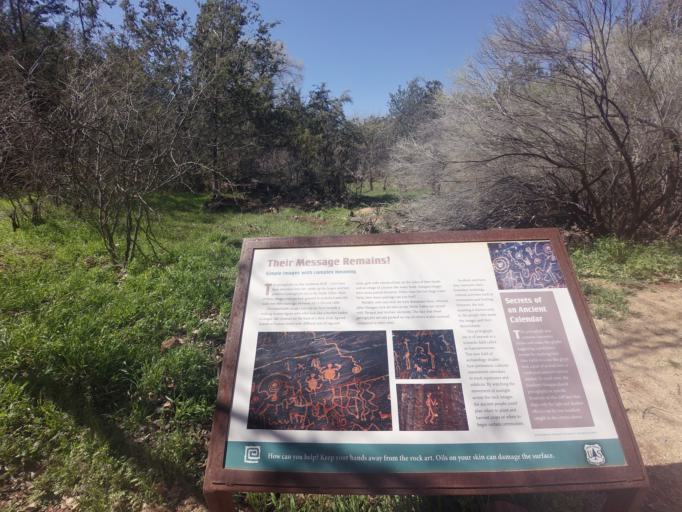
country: US
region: Arizona
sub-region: Yavapai County
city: Lake Montezuma
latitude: 34.6606
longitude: -111.7190
